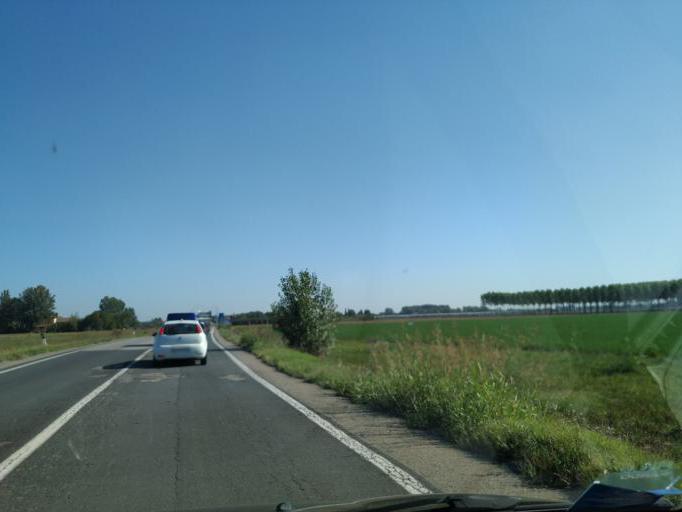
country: IT
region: Emilia-Romagna
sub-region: Provincia di Bologna
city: Decima
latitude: 44.7131
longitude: 11.2437
